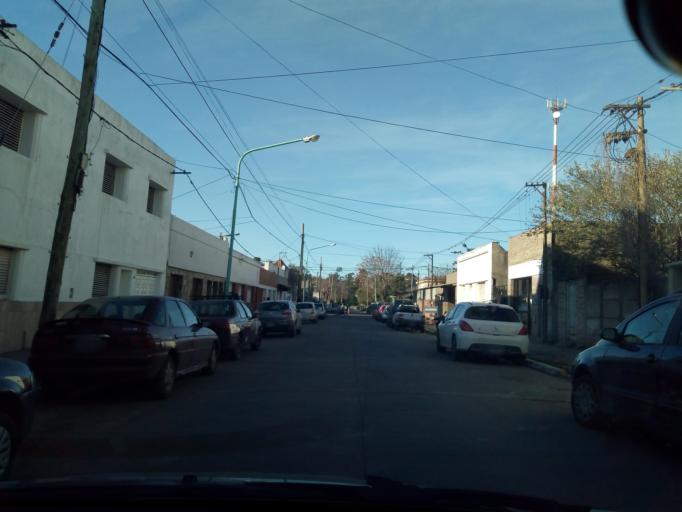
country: AR
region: Buenos Aires
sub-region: Partido de Ensenada
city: Ensenada
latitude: -34.8586
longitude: -57.9051
